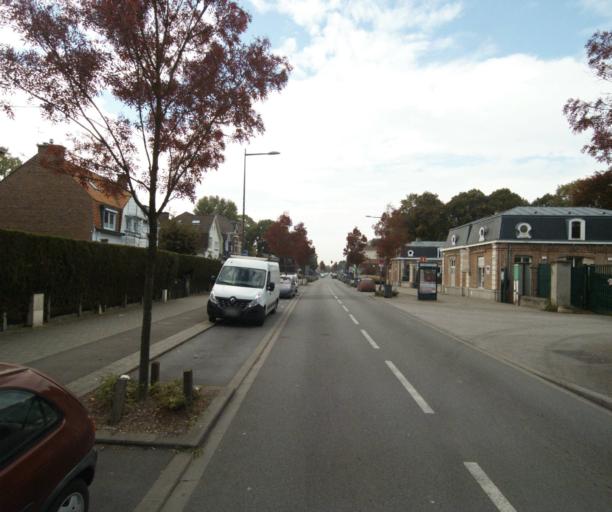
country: FR
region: Nord-Pas-de-Calais
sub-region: Departement du Nord
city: Seclin
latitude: 50.5460
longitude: 3.0260
